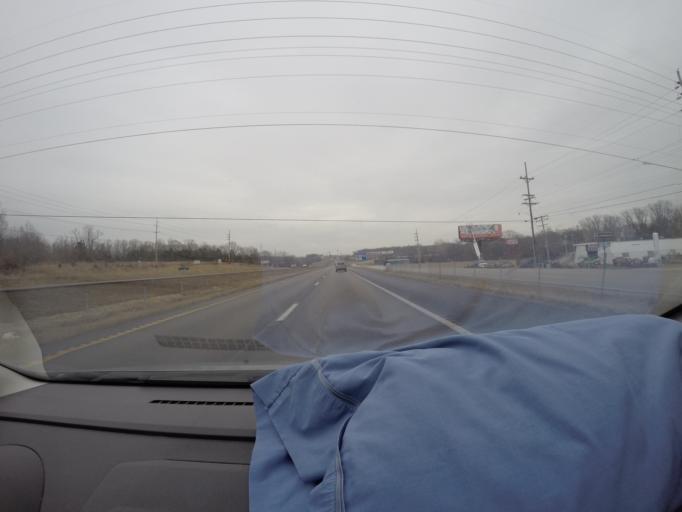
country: US
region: Missouri
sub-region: Warren County
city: Warrenton
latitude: 38.8205
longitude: -91.1566
